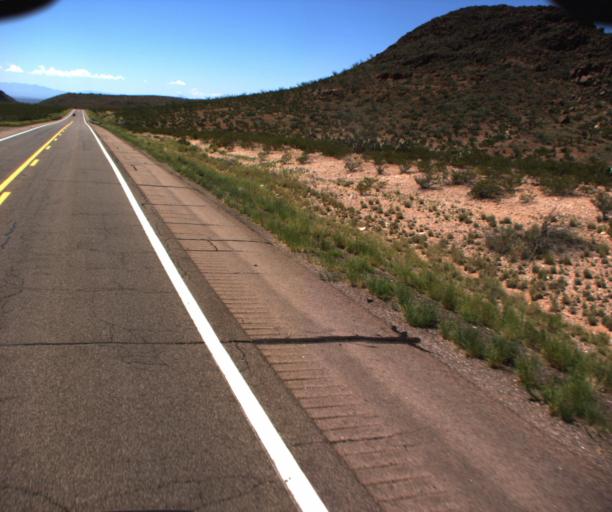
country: US
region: Arizona
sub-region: Greenlee County
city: Clifton
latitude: 32.8463
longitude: -109.3746
